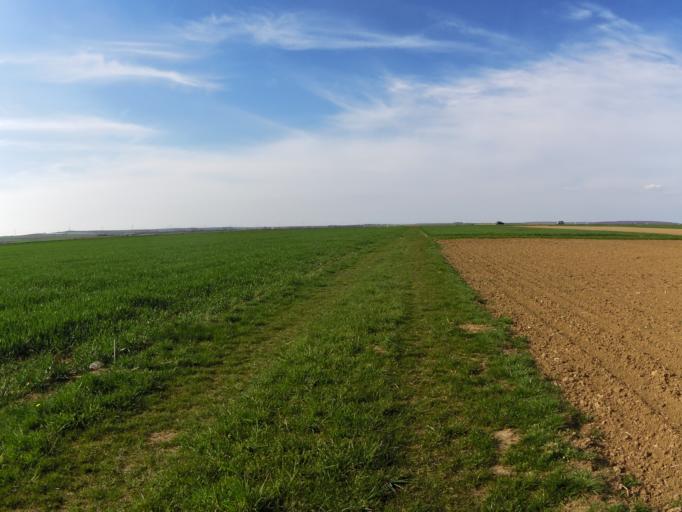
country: DE
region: Bavaria
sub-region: Regierungsbezirk Unterfranken
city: Mainstockheim
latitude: 49.7932
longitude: 10.1266
